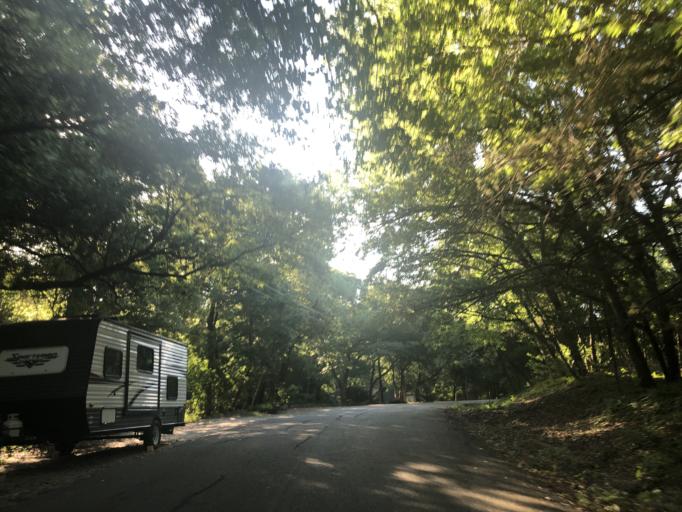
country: US
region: Texas
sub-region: Dallas County
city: Duncanville
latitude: 32.6709
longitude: -96.9143
